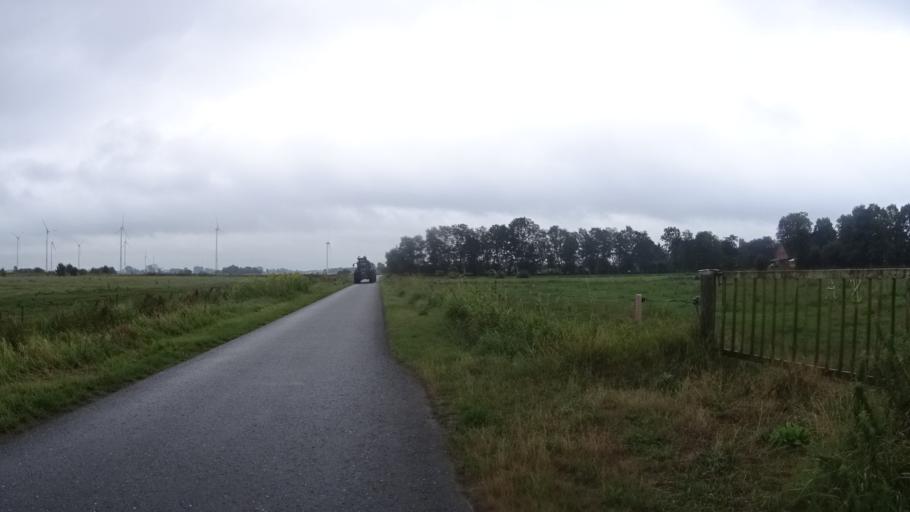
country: DE
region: Lower Saxony
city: Weener
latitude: 53.1804
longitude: 7.3181
